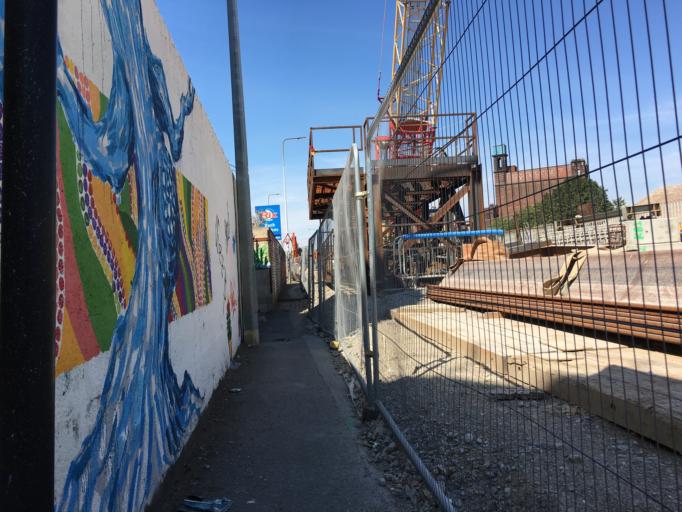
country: GB
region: England
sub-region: City of Kingston upon Hull
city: Hull
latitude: 53.7578
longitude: -0.3356
